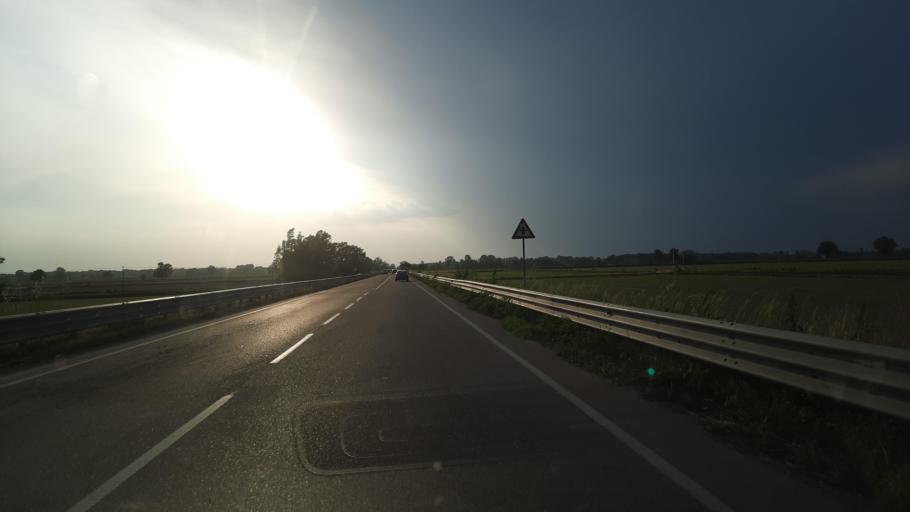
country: IT
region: Lombardy
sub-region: Provincia di Pavia
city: Tromello
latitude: 45.2231
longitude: 8.8354
